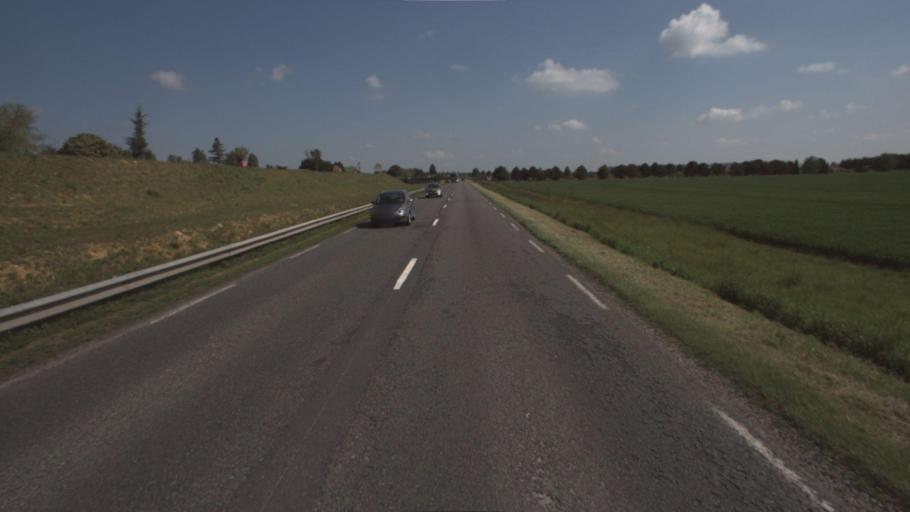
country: FR
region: Ile-de-France
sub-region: Departement de Seine-et-Marne
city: Moisenay
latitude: 48.6108
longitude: 2.7445
